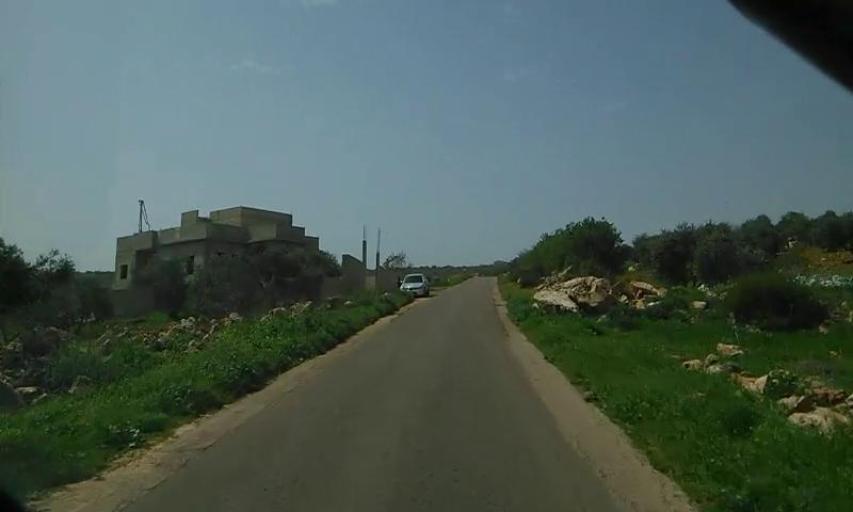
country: PS
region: West Bank
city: At Taybah
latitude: 32.4979
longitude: 35.1922
